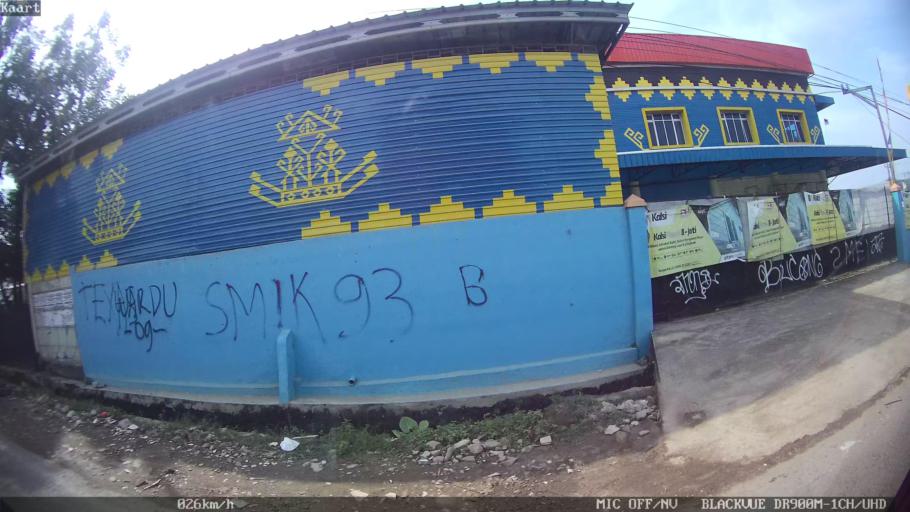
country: ID
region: Lampung
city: Kedaton
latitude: -5.3892
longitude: 105.2886
